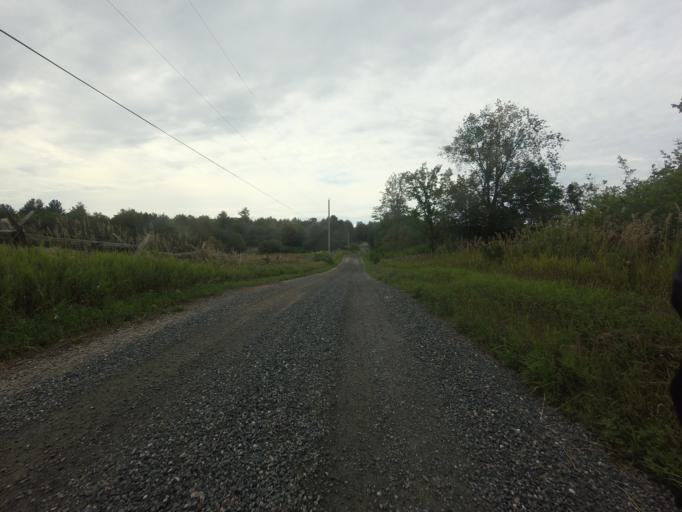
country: CA
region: Ontario
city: Perth
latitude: 45.0581
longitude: -76.3933
